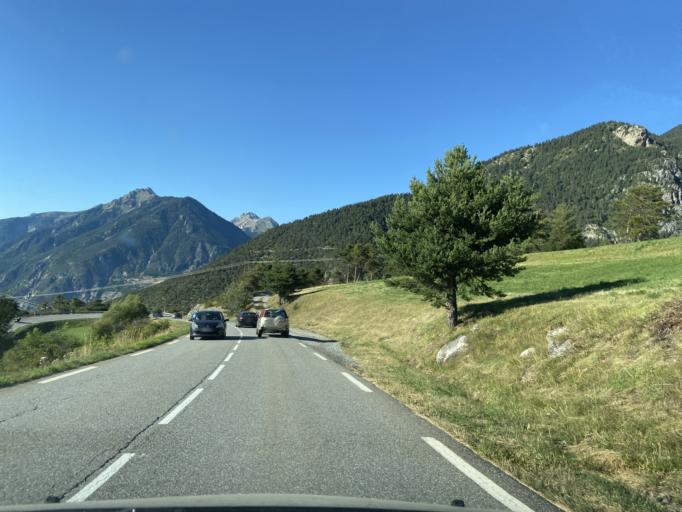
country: FR
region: Provence-Alpes-Cote d'Azur
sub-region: Departement des Hautes-Alpes
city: Guillestre
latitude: 44.6358
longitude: 6.6700
